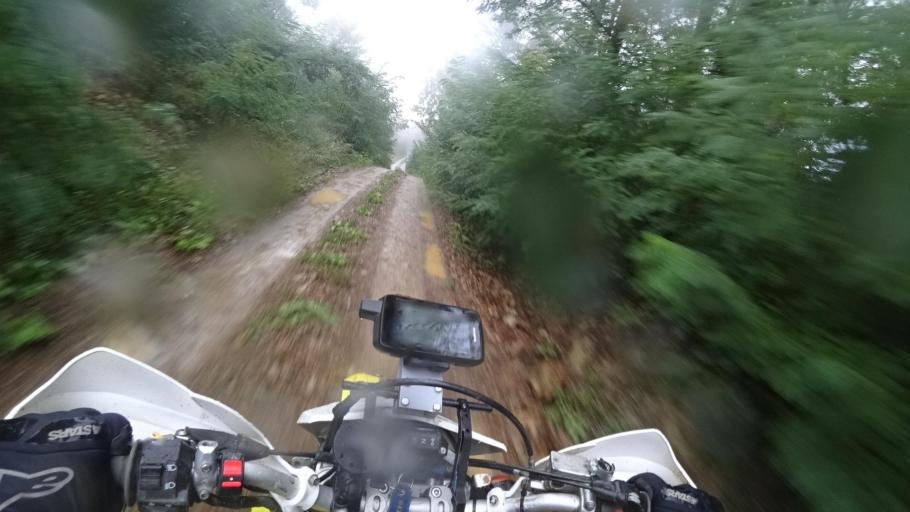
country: BA
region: Republika Srpska
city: Maricka
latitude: 44.8189
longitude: 16.7826
